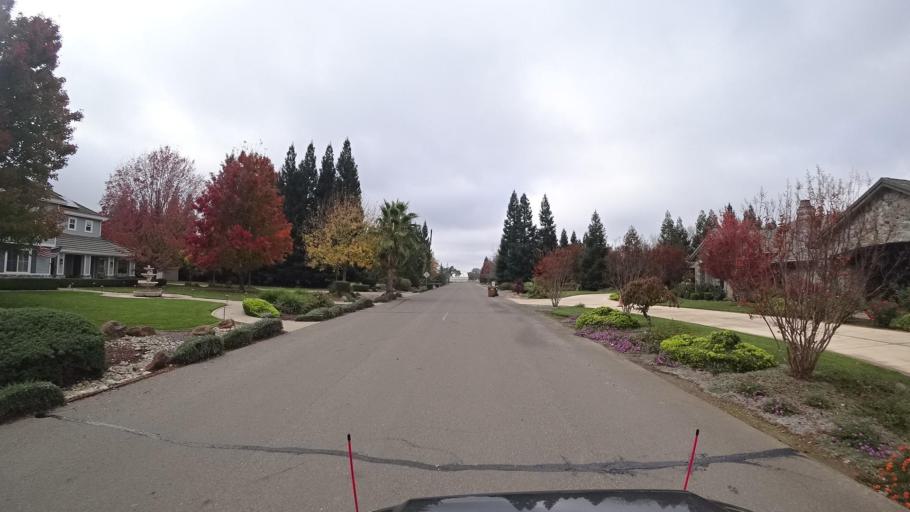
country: US
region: California
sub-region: Sacramento County
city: Wilton
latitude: 38.4391
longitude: -121.2998
